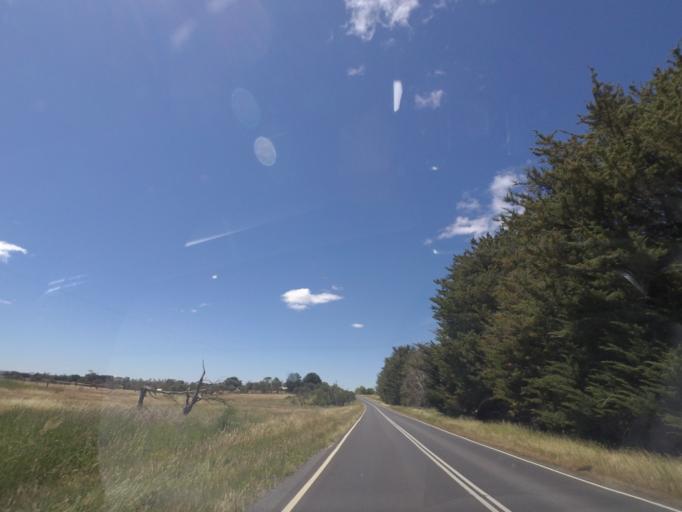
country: AU
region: Victoria
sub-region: Mount Alexander
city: Castlemaine
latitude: -37.2433
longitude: 144.3247
